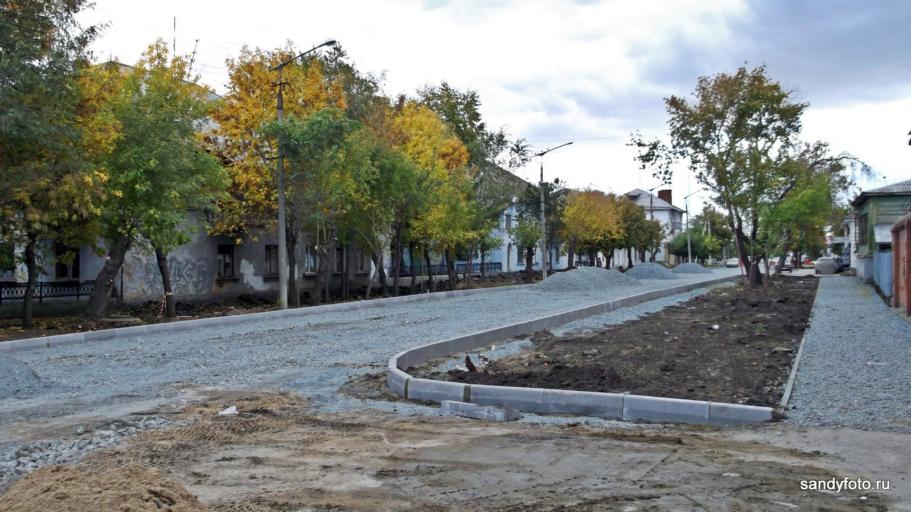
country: RU
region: Chelyabinsk
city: Troitsk
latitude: 54.0891
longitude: 61.5546
